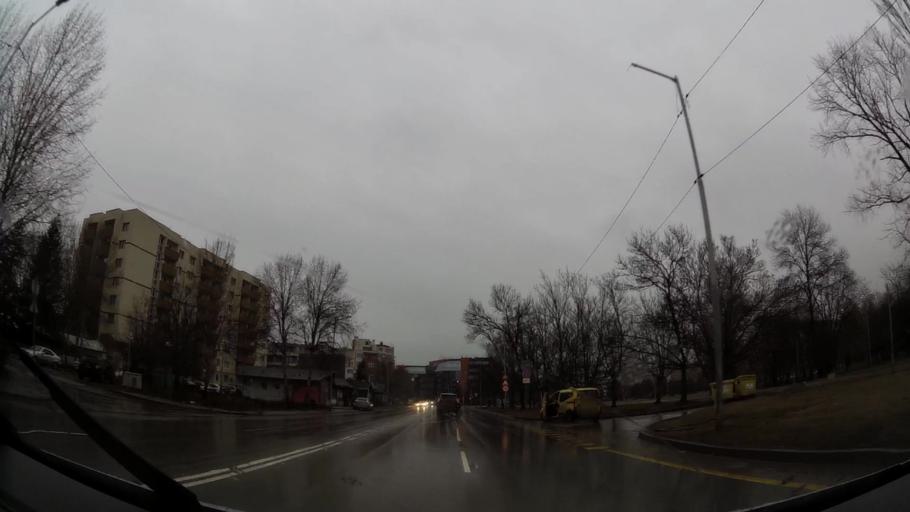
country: BG
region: Sofia-Capital
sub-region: Stolichna Obshtina
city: Sofia
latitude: 42.6552
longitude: 23.3495
